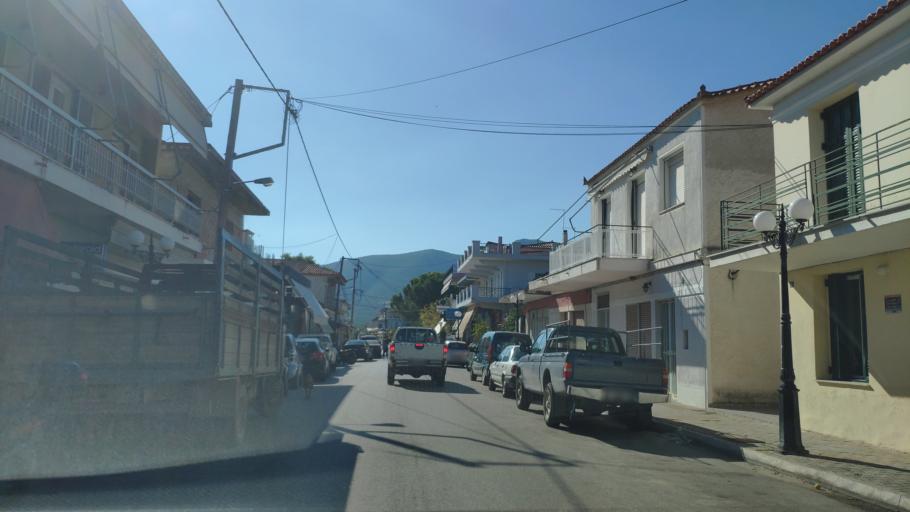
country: GR
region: Peloponnese
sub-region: Nomos Korinthias
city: Khiliomodhi
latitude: 37.8091
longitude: 22.8698
